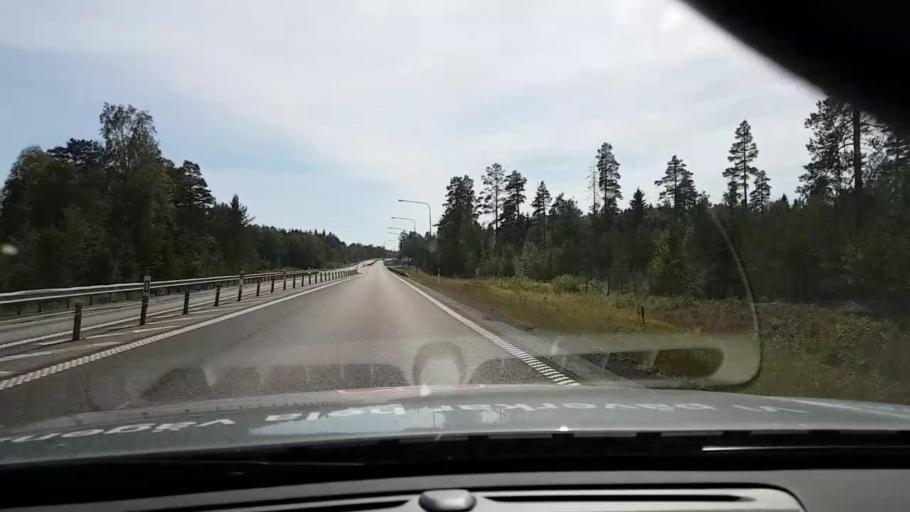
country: SE
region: Vaesternorrland
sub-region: OErnskoeldsviks Kommun
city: Husum
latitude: 63.3771
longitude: 19.1904
